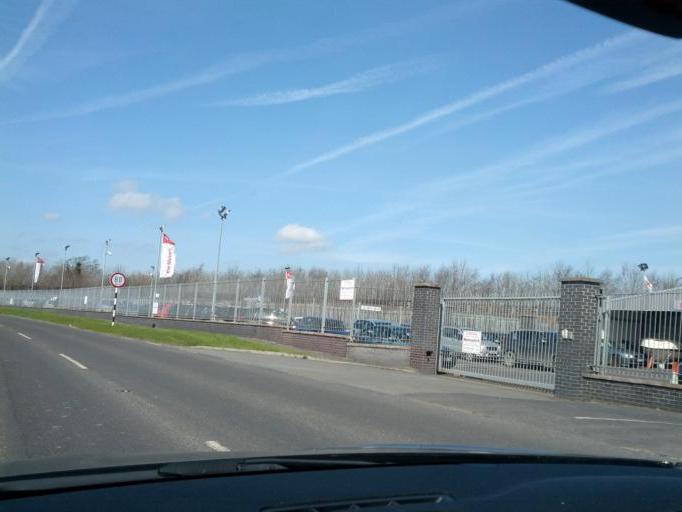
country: IE
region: Leinster
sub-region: Kildare
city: Celbridge
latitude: 53.3627
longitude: -6.5574
